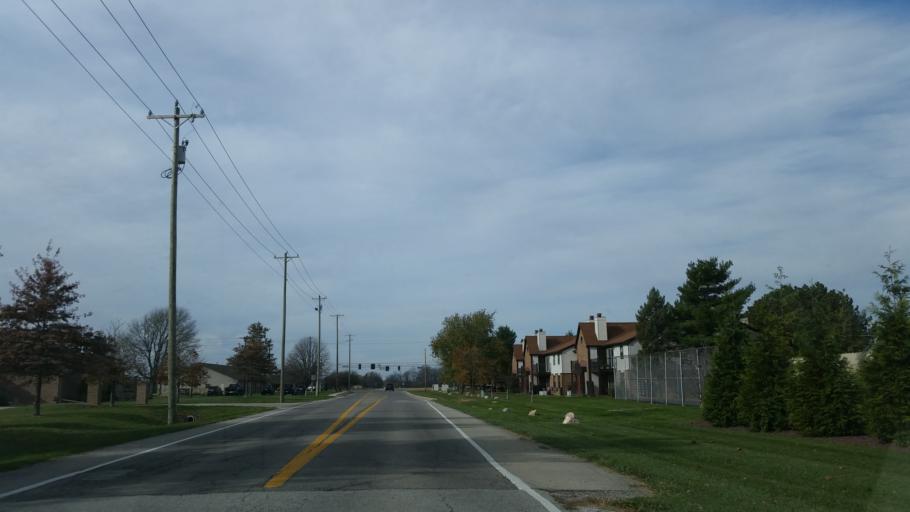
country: US
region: Indiana
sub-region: Howard County
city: Indian Heights
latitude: 40.4473
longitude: -86.1626
